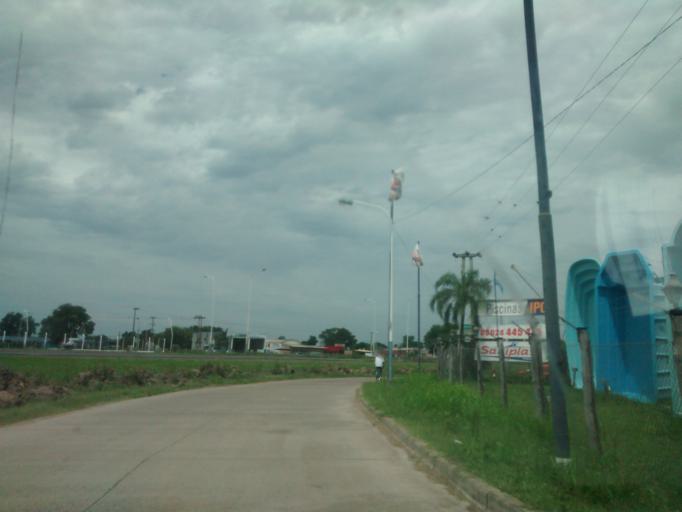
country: AR
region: Chaco
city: Resistencia
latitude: -27.4158
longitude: -58.9687
